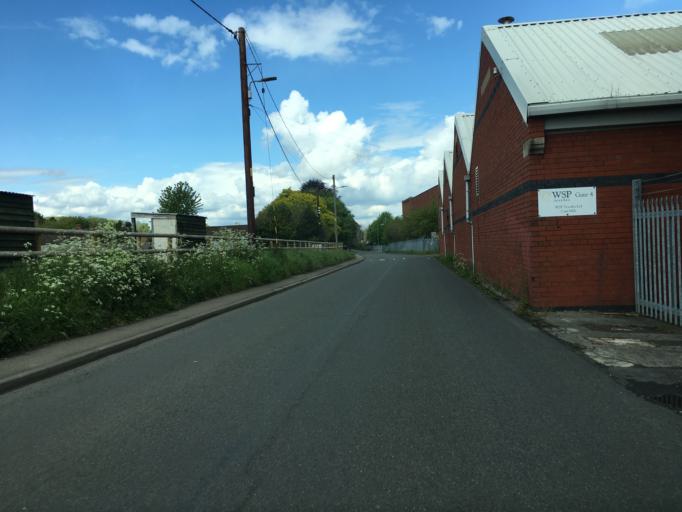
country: GB
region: England
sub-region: Gloucestershire
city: Dursley
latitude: 51.6970
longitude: -2.3581
